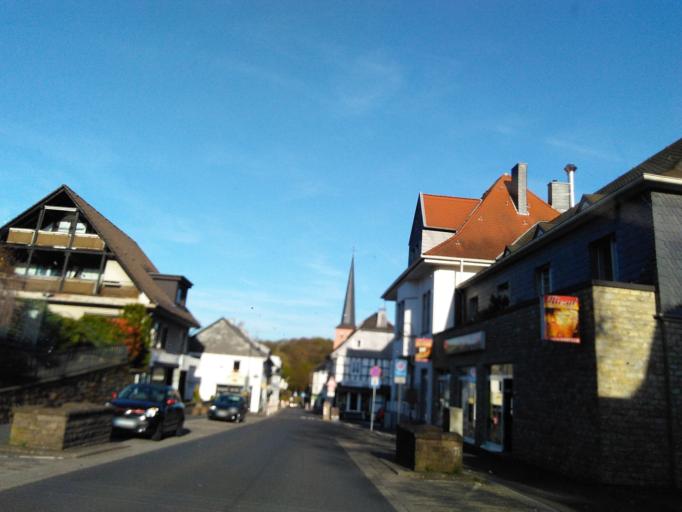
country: DE
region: North Rhine-Westphalia
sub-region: Regierungsbezirk Koln
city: Much
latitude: 50.9054
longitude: 7.4054
